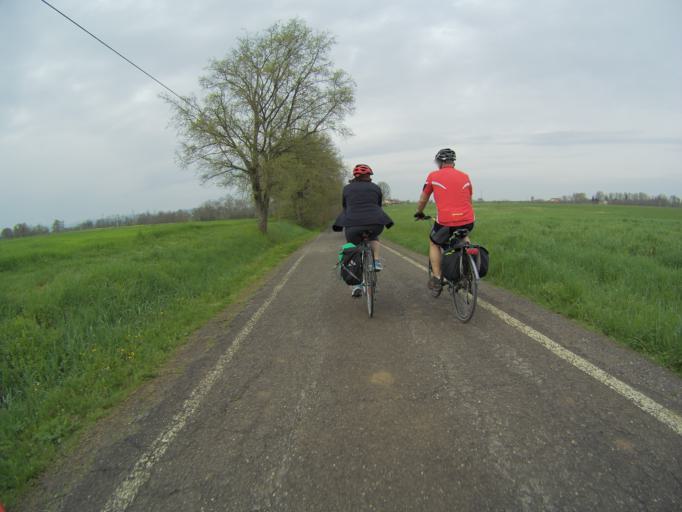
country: IT
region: Emilia-Romagna
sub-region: Provincia di Reggio Emilia
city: San Bartolomeo
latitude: 44.6656
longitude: 10.5566
